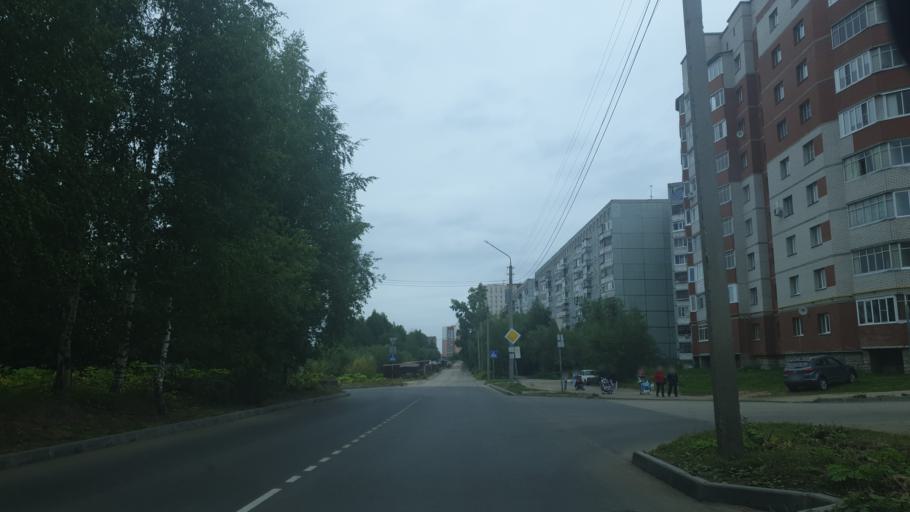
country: RU
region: Komi Republic
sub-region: Syktyvdinskiy Rayon
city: Syktyvkar
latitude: 61.6958
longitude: 50.8068
